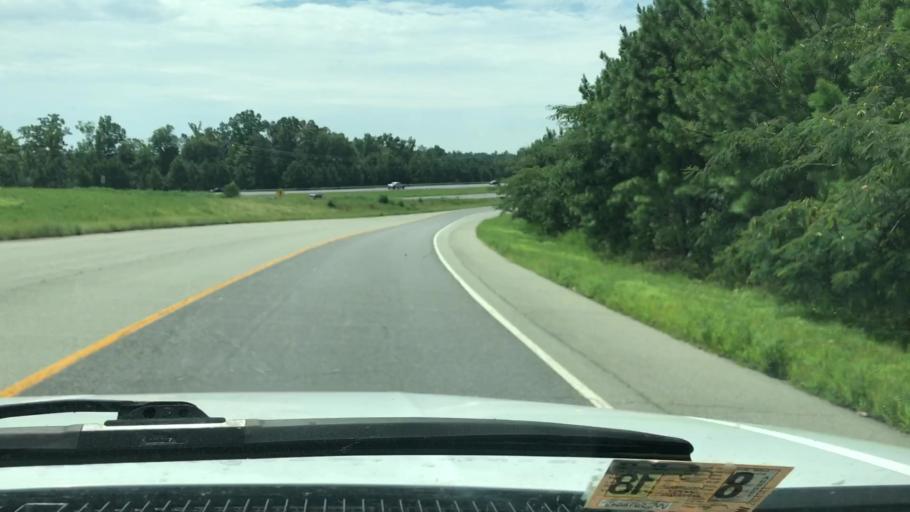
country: US
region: Virginia
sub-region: Henrico County
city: Short Pump
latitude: 37.5971
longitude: -77.6689
